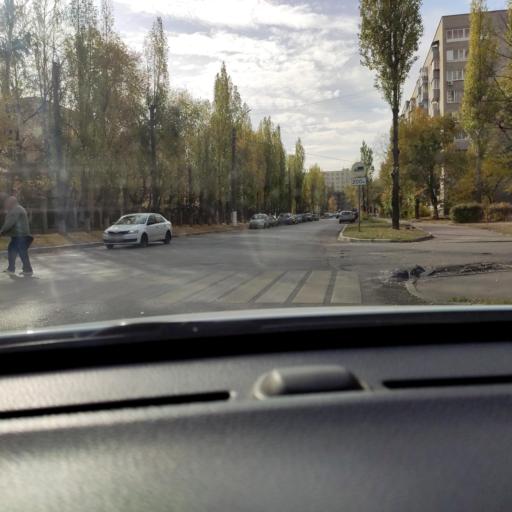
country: RU
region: Voronezj
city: Pridonskoy
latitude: 51.6566
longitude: 39.1178
